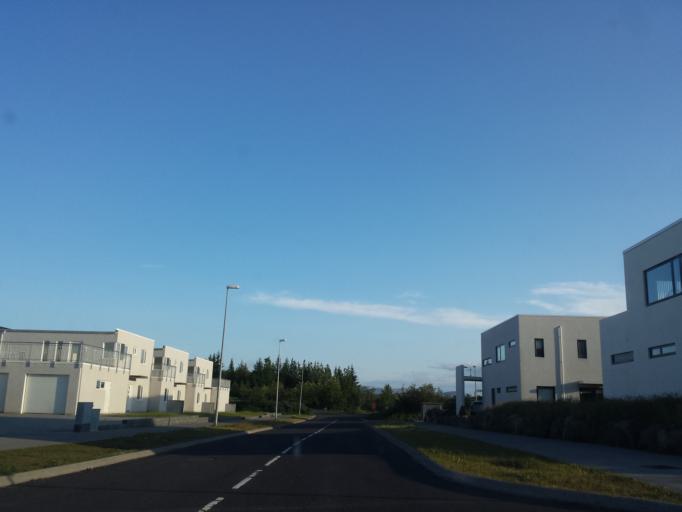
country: IS
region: Capital Region
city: Mosfellsbaer
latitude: 64.0963
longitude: -21.7781
